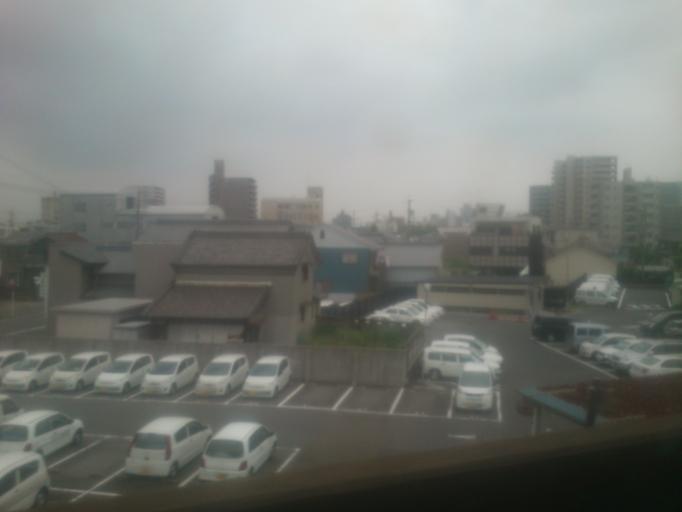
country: JP
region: Aichi
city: Ichinomiya
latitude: 35.3074
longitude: 136.7948
